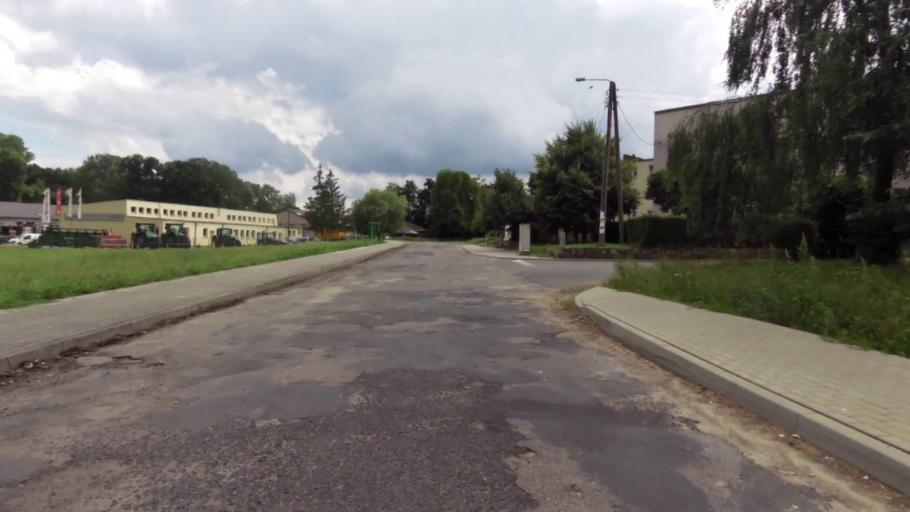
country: PL
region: West Pomeranian Voivodeship
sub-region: Powiat pyrzycki
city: Lipiany
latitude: 52.9947
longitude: 15.0527
